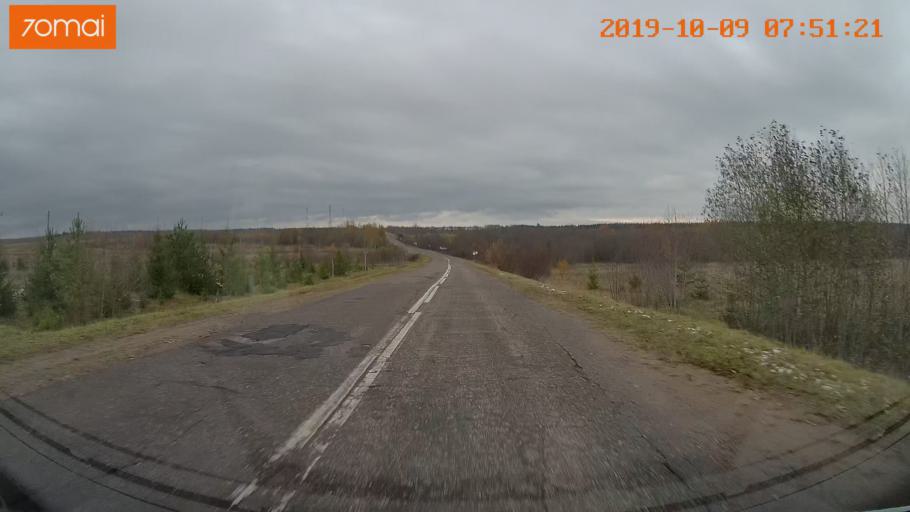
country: RU
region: Jaroslavl
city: Kukoboy
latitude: 58.6822
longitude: 39.8770
